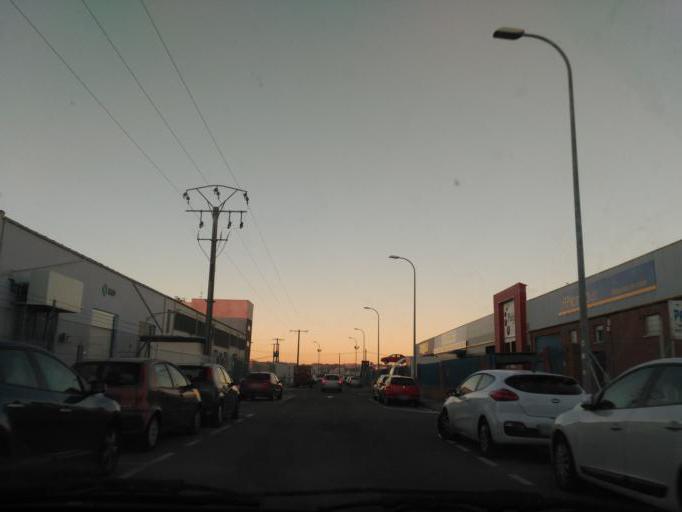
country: ES
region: Castille and Leon
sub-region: Provincia de Salamanca
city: Carbajosa de la Sagrada
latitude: 40.9465
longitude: -5.6529
